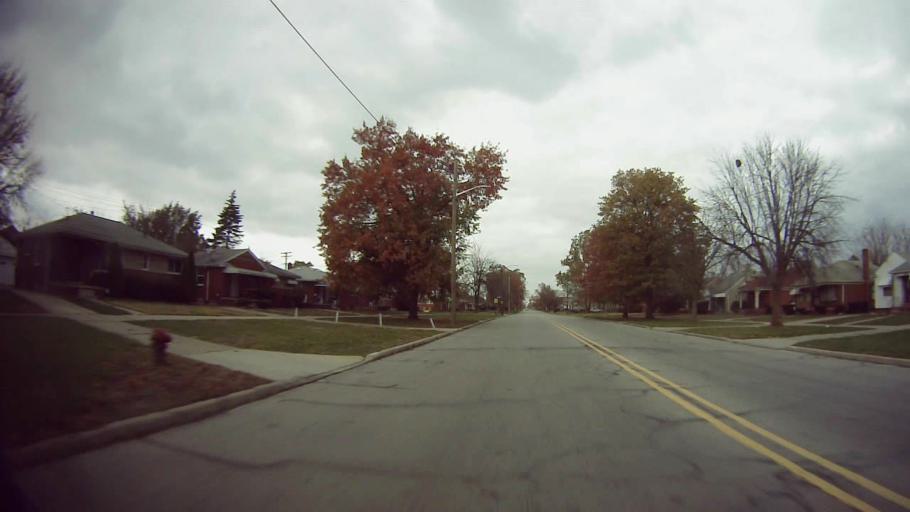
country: US
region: Michigan
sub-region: Wayne County
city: Hamtramck
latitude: 42.4246
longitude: -83.0042
